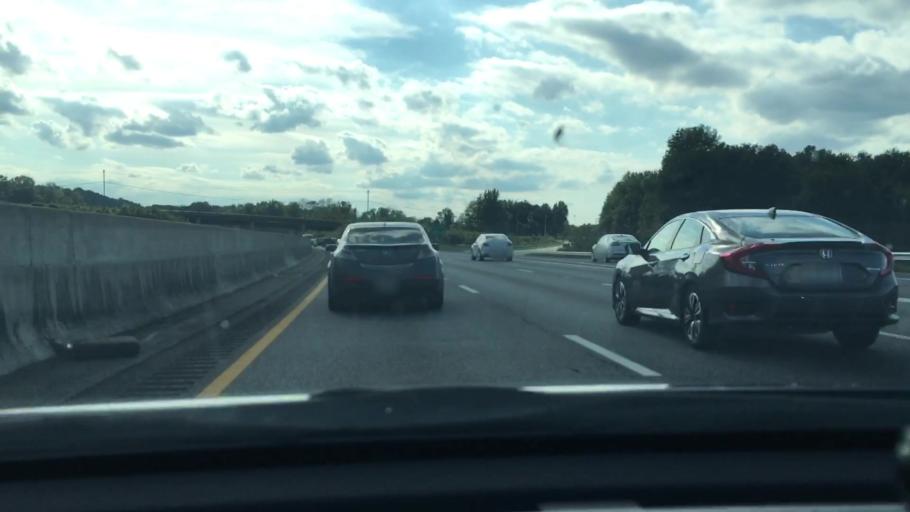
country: US
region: South Carolina
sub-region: Richland County
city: Columbia
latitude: 34.0650
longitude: -81.0432
